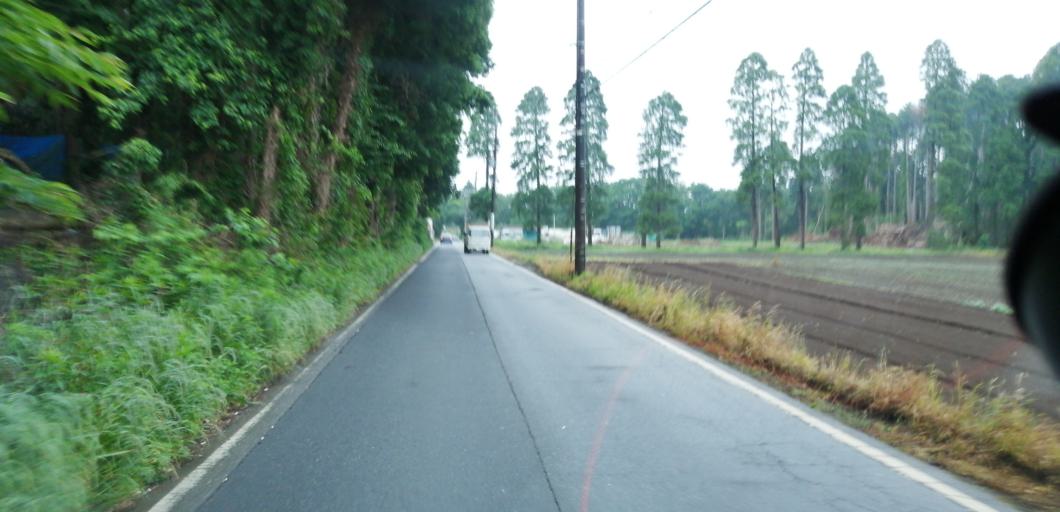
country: JP
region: Chiba
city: Oami
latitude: 35.5657
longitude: 140.2574
